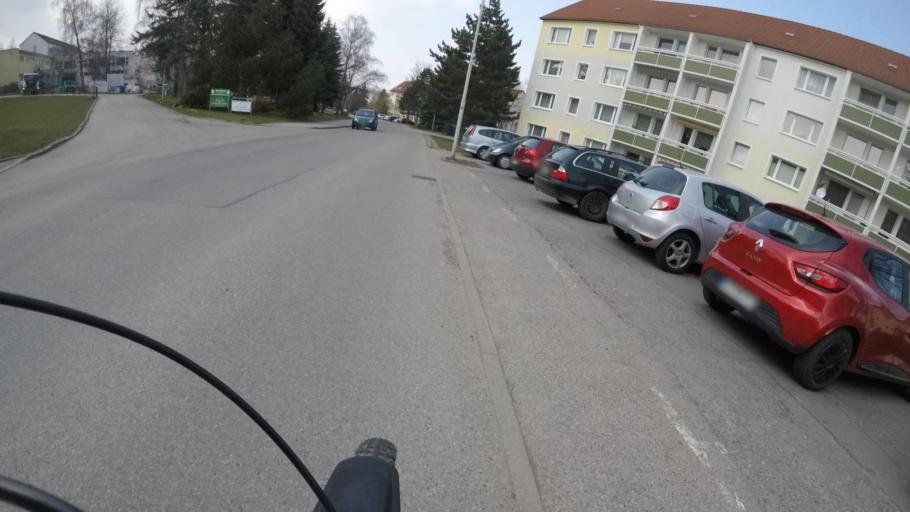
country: DE
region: Saxony
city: Limbach-Oberfrohna
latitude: 50.8640
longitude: 12.7682
